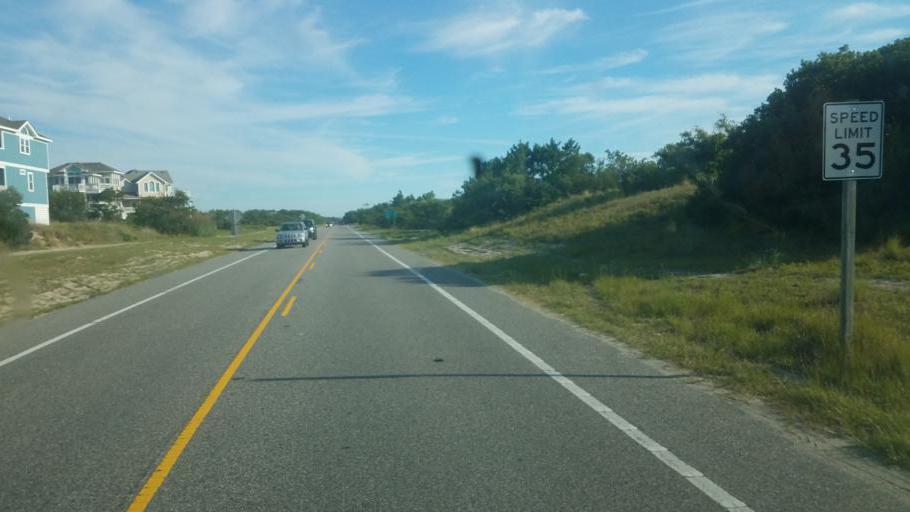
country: US
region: North Carolina
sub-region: Dare County
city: Southern Shores
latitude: 36.3313
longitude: -75.8164
